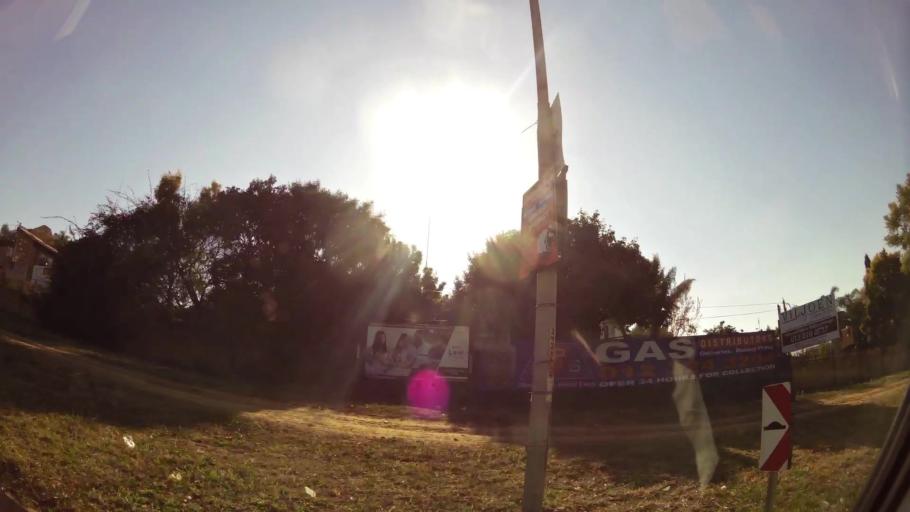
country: ZA
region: Gauteng
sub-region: City of Tshwane Metropolitan Municipality
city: Centurion
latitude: -25.8336
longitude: 28.2897
